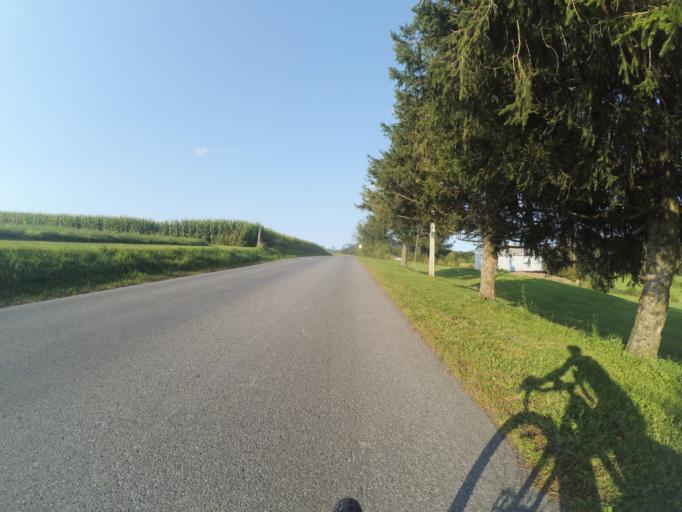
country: US
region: Pennsylvania
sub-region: Centre County
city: Centre Hall
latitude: 40.8013
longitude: -77.6443
